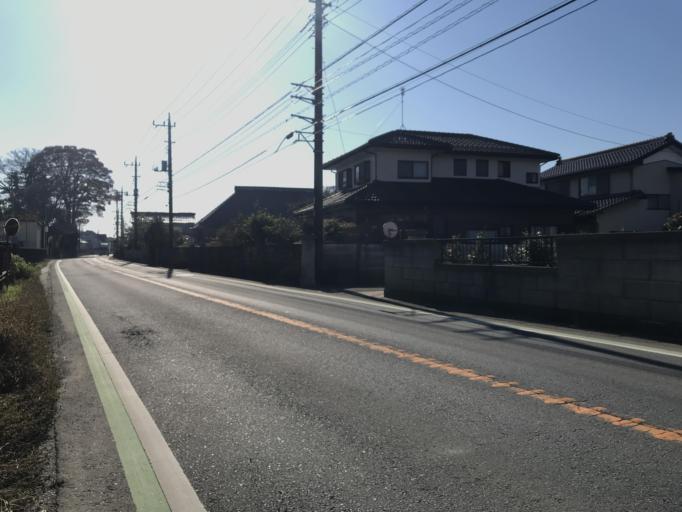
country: JP
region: Ibaraki
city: Sakai
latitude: 36.1758
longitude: 139.8087
